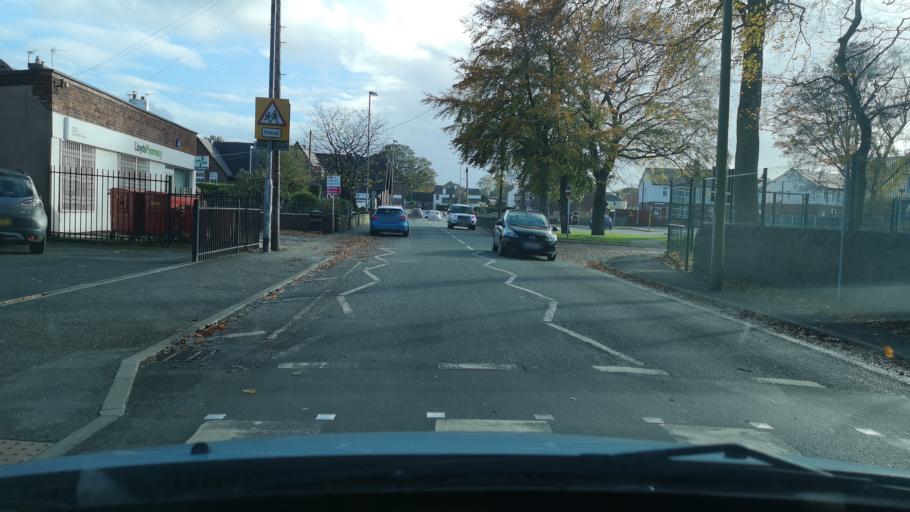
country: GB
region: England
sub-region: City and Borough of Wakefield
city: Crofton
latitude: 53.6560
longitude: -1.4282
